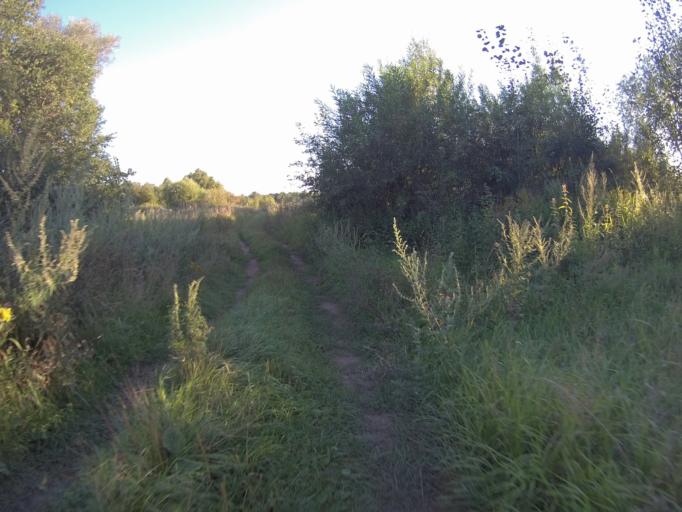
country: RU
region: Vladimir
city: Vladimir
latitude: 56.0787
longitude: 40.3918
